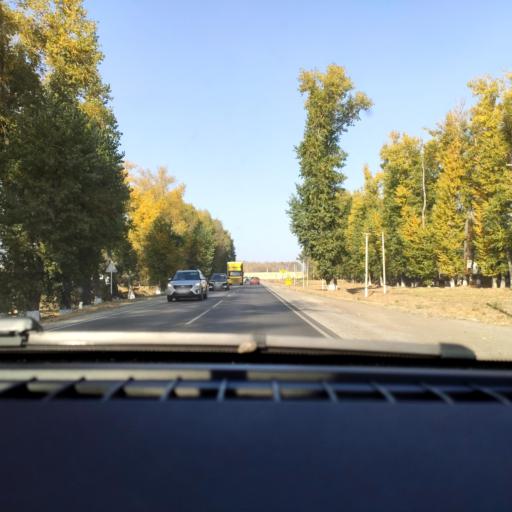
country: RU
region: Voronezj
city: Novaya Usman'
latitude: 51.6759
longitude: 39.4061
